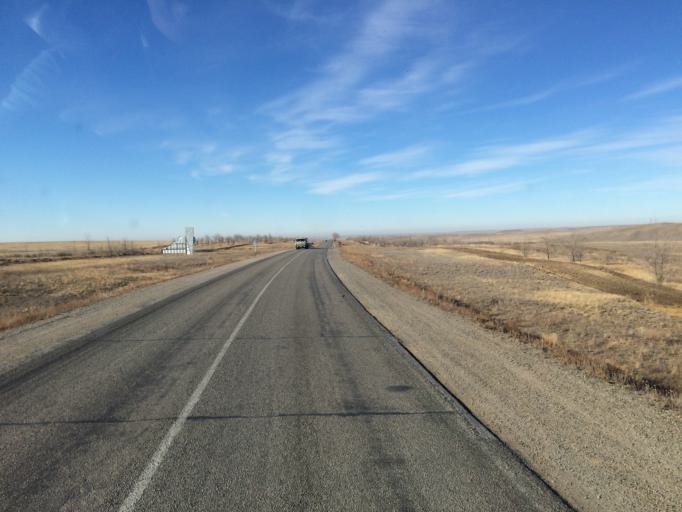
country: KZ
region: Aqtoebe
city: Aqtobe
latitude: 50.2819
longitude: 57.7471
